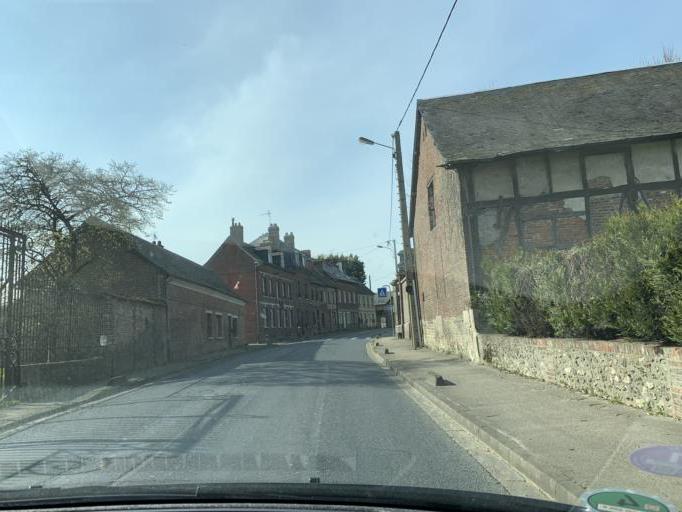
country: FR
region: Haute-Normandie
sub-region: Departement de l'Eure
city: Les Andelys
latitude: 49.3090
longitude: 1.4344
